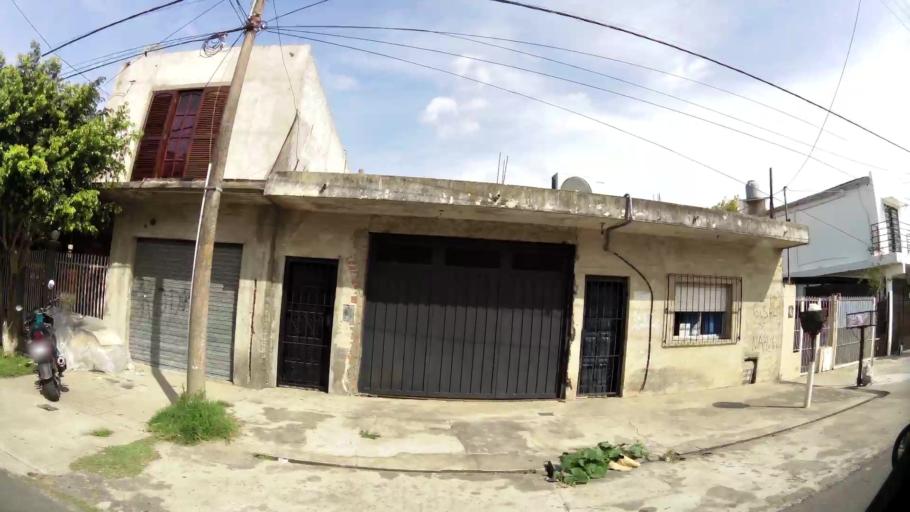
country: AR
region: Buenos Aires
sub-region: Partido de Quilmes
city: Quilmes
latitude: -34.7628
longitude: -58.2380
